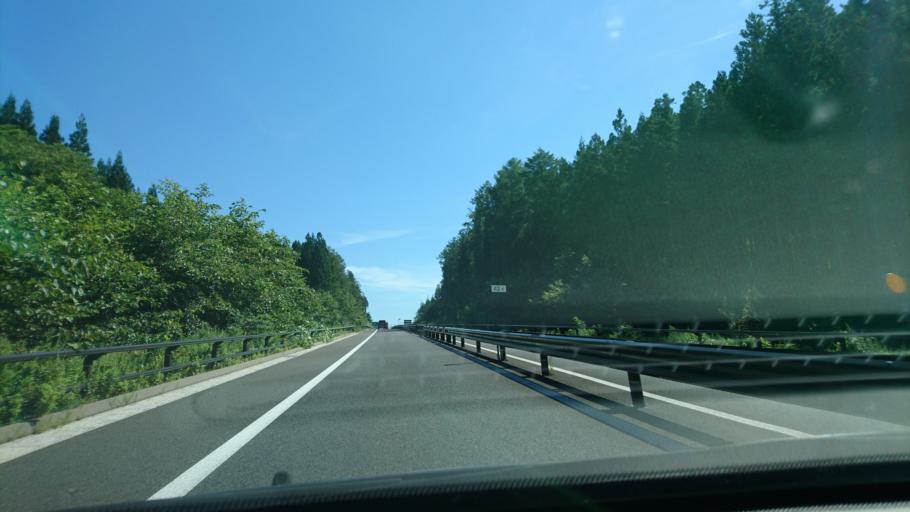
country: JP
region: Iwate
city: Tono
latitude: 39.3221
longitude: 141.4832
